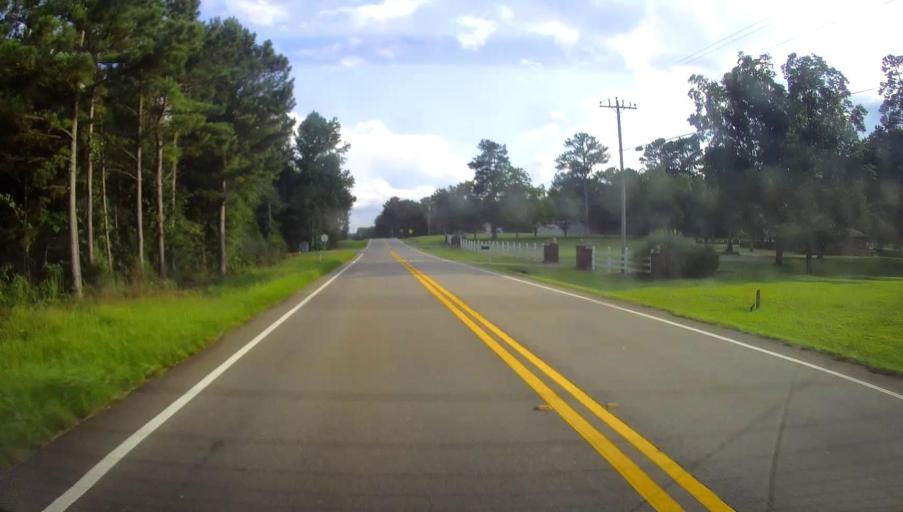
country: US
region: Georgia
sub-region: Monroe County
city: Forsyth
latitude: 32.9798
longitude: -83.9527
